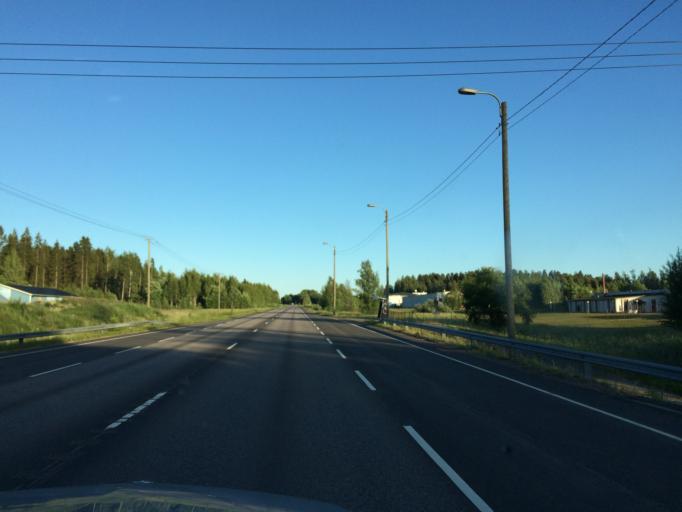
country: FI
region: Haeme
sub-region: Haemeenlinna
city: Tervakoski
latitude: 60.8141
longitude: 24.6443
